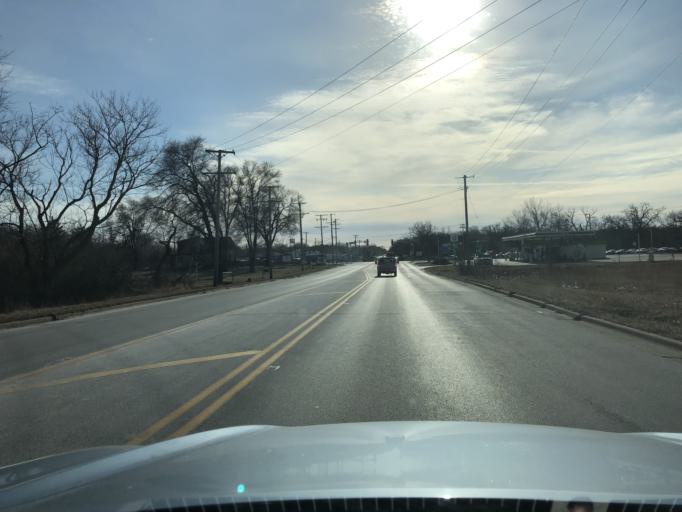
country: US
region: Illinois
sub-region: Lake County
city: Third Lake
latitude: 42.3878
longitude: -88.0042
